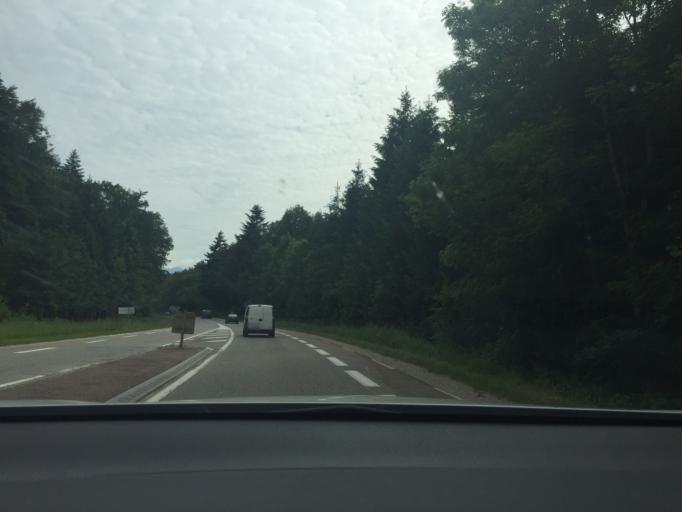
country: FR
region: Rhone-Alpes
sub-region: Departement de la Savoie
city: Les Echelles
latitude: 45.4692
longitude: 5.8168
